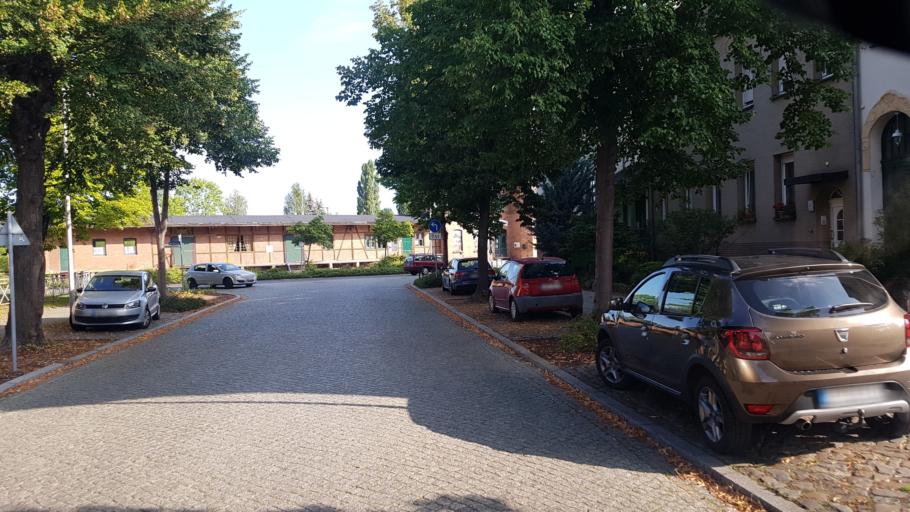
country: DE
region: Brandenburg
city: Luckau
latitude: 51.8570
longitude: 13.7143
